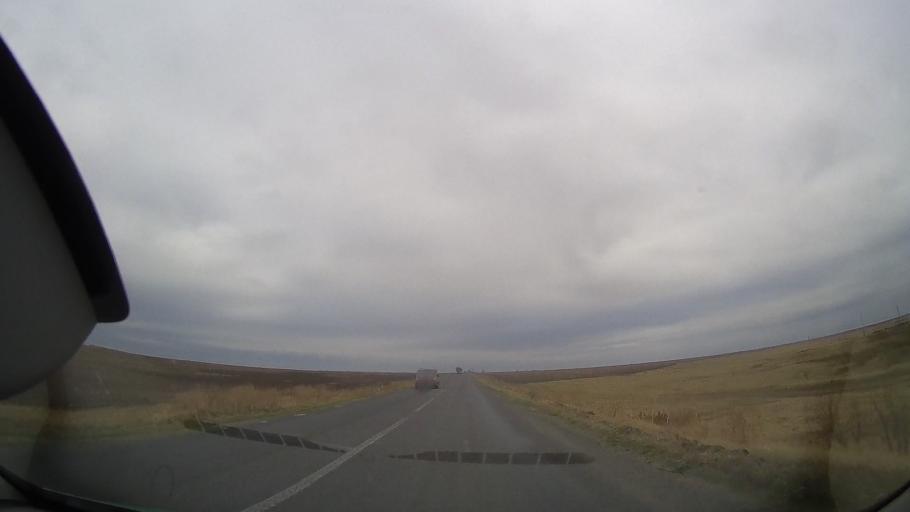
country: RO
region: Buzau
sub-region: Comuna Padina
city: Padina
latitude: 44.8157
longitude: 27.1227
